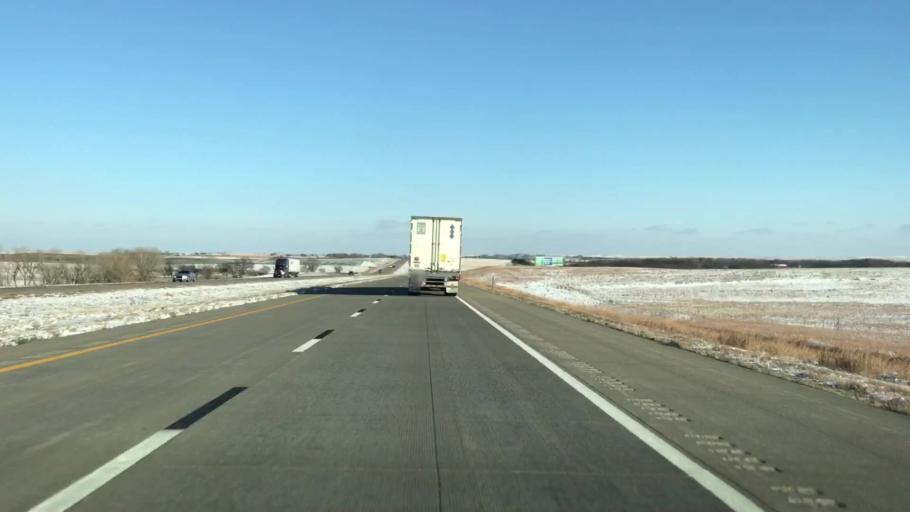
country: US
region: Kansas
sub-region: Lincoln County
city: Lincoln
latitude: 38.8782
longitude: -98.0023
